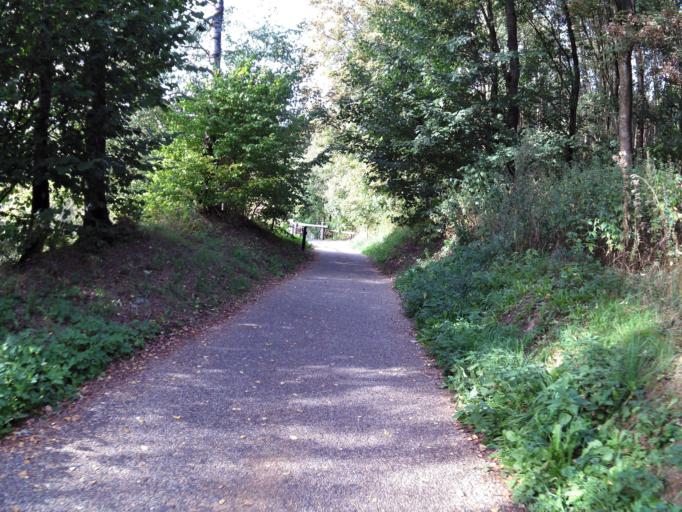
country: BE
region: Wallonia
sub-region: Province de Liege
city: Saint-Vith
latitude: 50.2731
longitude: 6.1382
